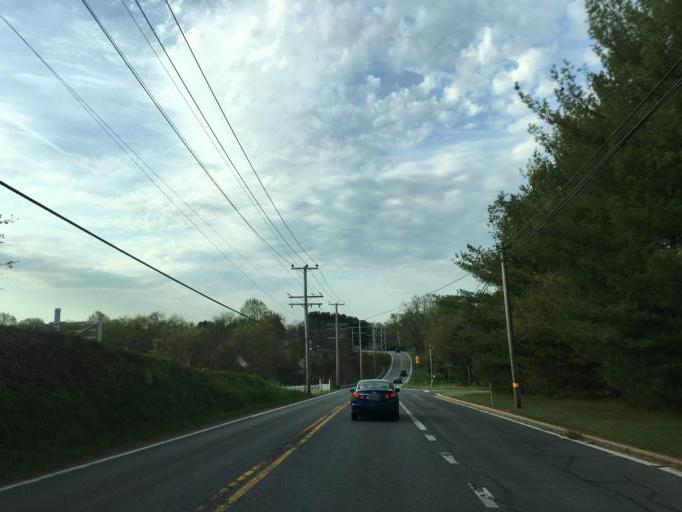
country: US
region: Maryland
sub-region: Carroll County
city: Eldersburg
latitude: 39.4543
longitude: -76.9279
